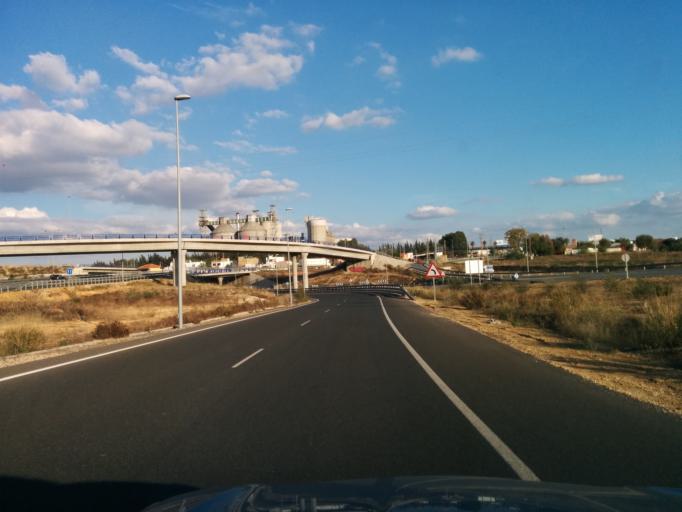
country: ES
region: Andalusia
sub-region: Provincia de Sevilla
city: Alcala de Guadaira
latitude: 37.3601
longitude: -5.8743
